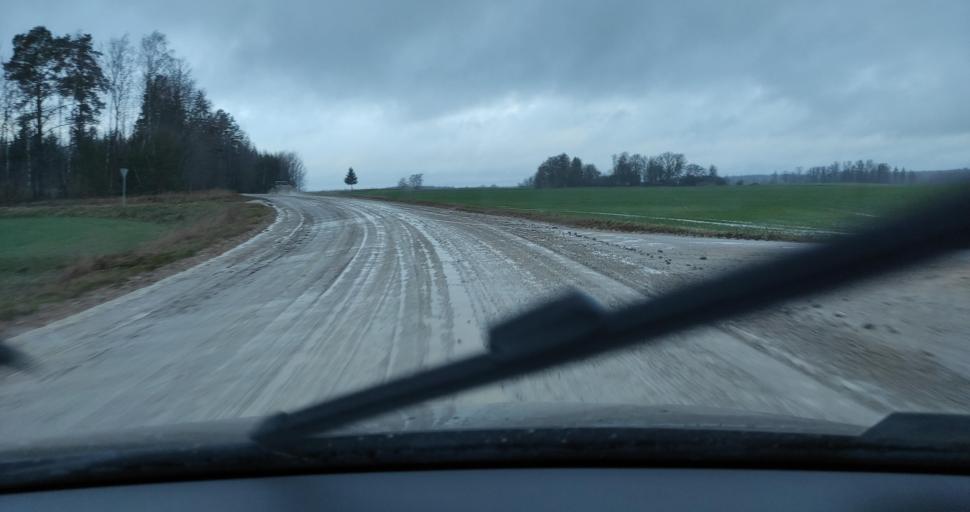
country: LV
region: Skrunda
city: Skrunda
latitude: 56.6941
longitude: 22.2192
